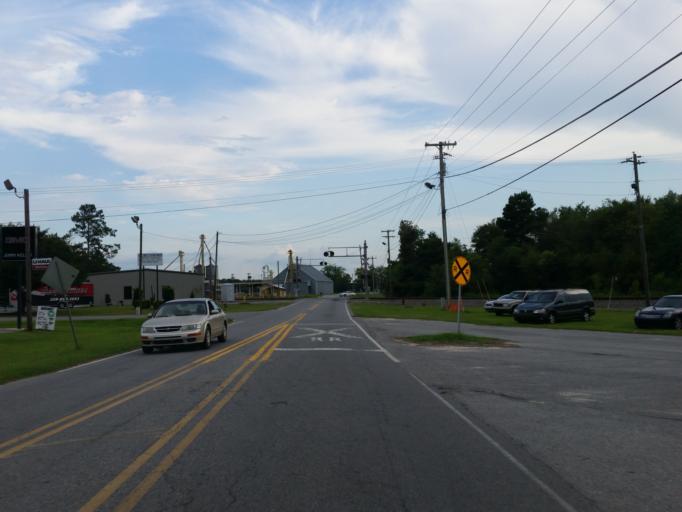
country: US
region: Georgia
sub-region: Cook County
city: Adel
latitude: 31.1219
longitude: -83.4189
